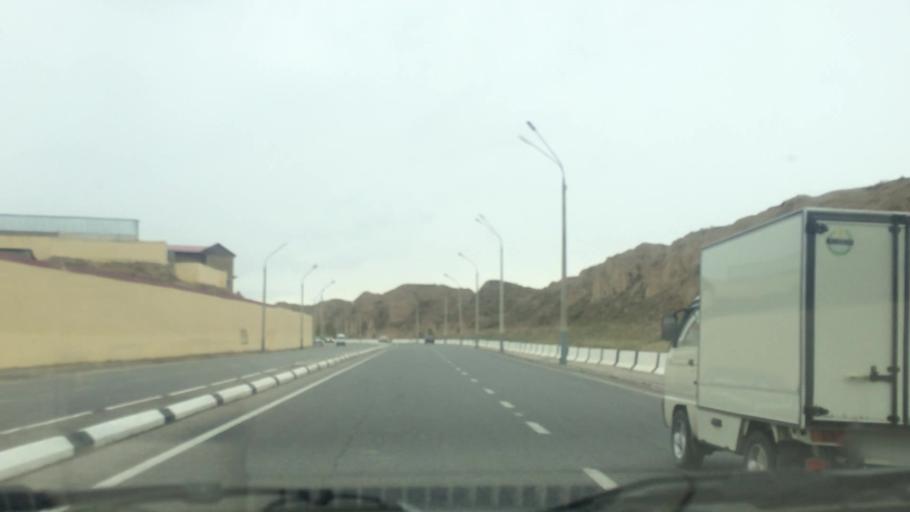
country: UZ
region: Samarqand
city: Samarqand
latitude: 39.6685
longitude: 66.9970
